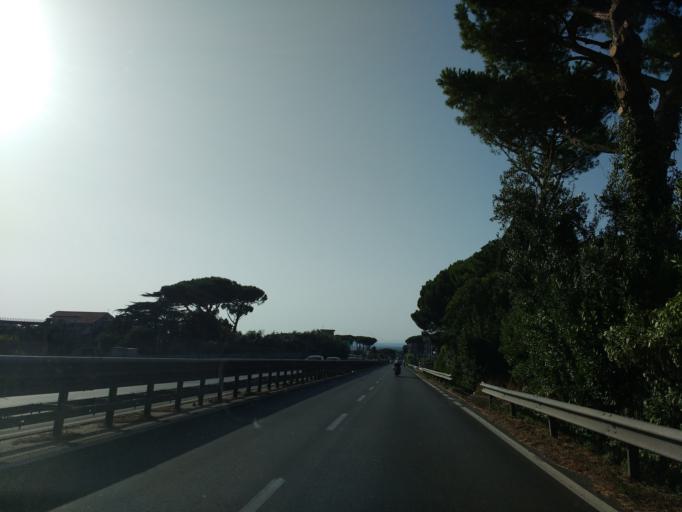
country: IT
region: Latium
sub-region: Citta metropolitana di Roma Capitale
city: Marino
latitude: 41.7578
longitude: 12.6263
